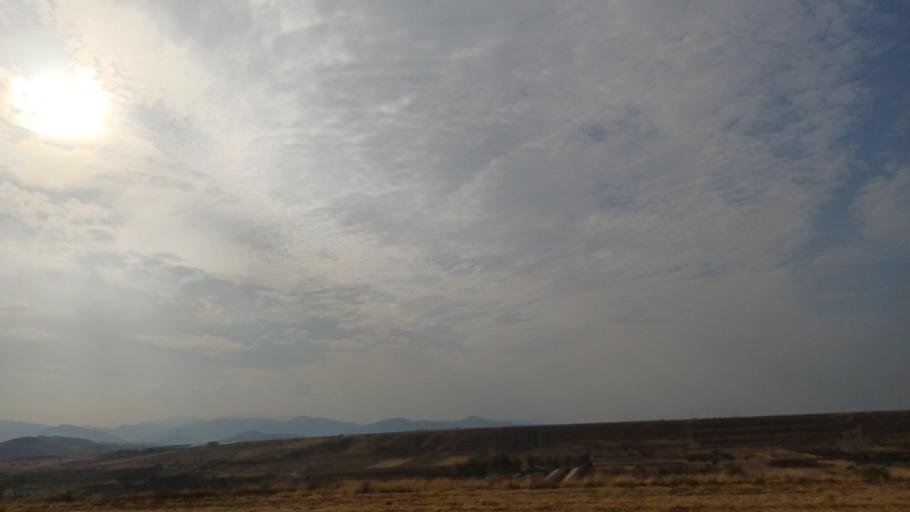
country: CY
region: Lefkosia
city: Peristerona
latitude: 35.0889
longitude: 33.0938
